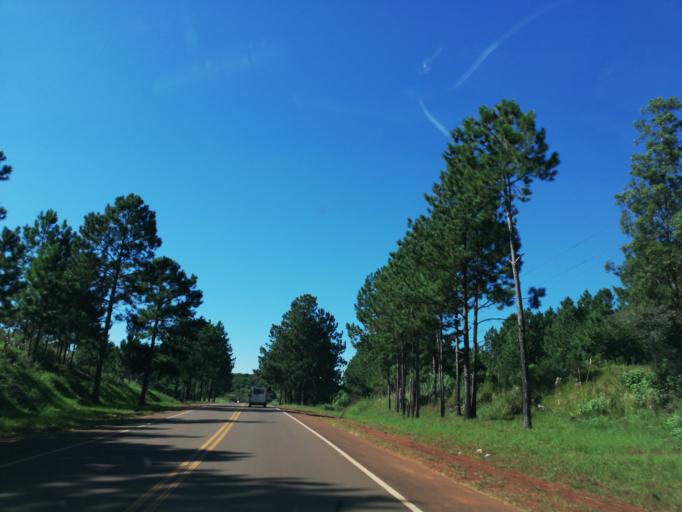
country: AR
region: Misiones
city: Dos de Mayo
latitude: -27.0496
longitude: -54.4336
